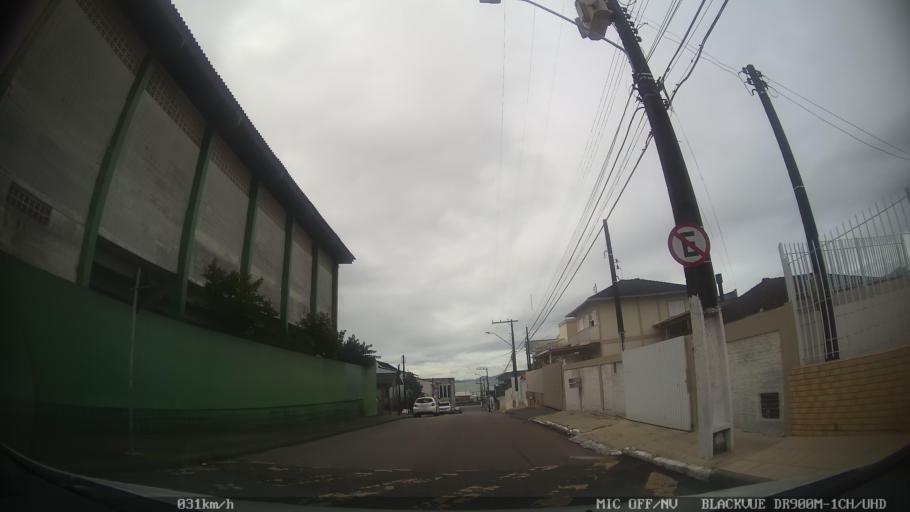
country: BR
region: Santa Catarina
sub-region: Biguacu
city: Biguacu
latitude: -27.5356
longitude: -48.6304
